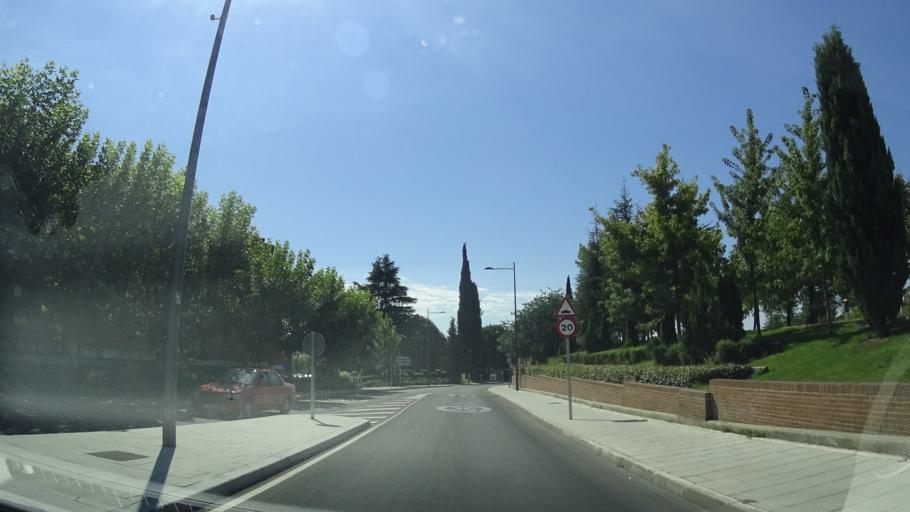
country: ES
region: Madrid
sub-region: Provincia de Madrid
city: Boadilla del Monte
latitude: 40.4045
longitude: -3.8776
